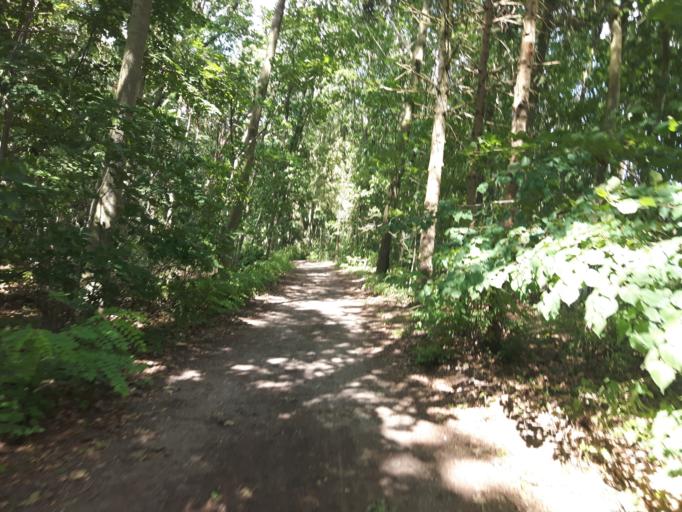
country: NL
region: Overijssel
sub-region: Gemeente Haaksbergen
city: Haaksbergen
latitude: 52.1872
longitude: 6.7652
